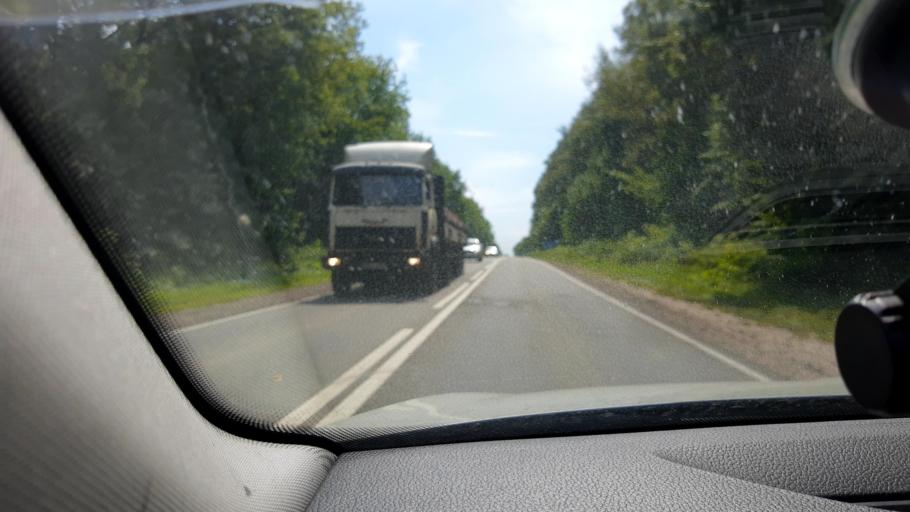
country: RU
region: Tula
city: Zaokskiy
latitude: 54.7908
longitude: 37.4331
